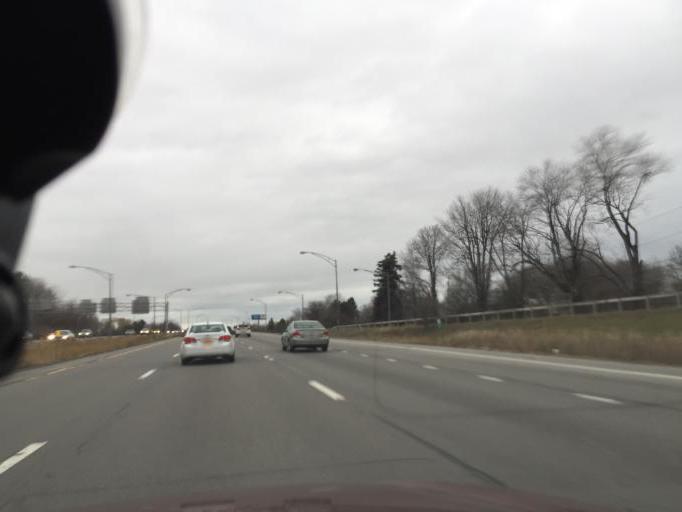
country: US
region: New York
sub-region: Monroe County
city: North Gates
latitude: 43.1657
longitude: -77.6828
